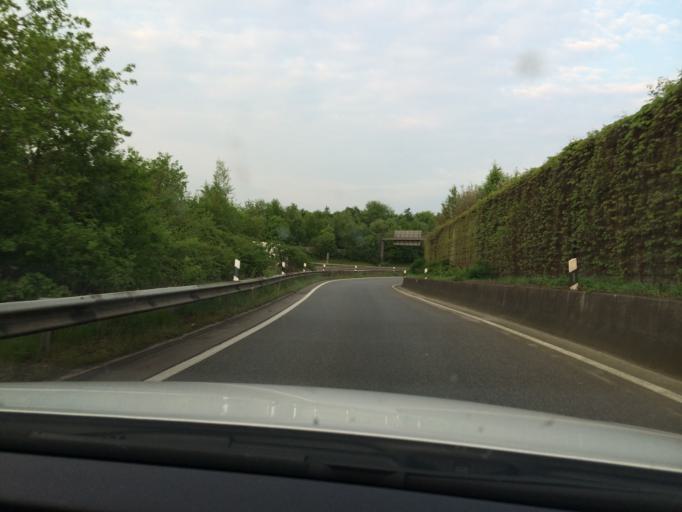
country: DE
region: Lower Saxony
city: Delmenhorst
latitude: 53.0367
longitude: 8.5899
